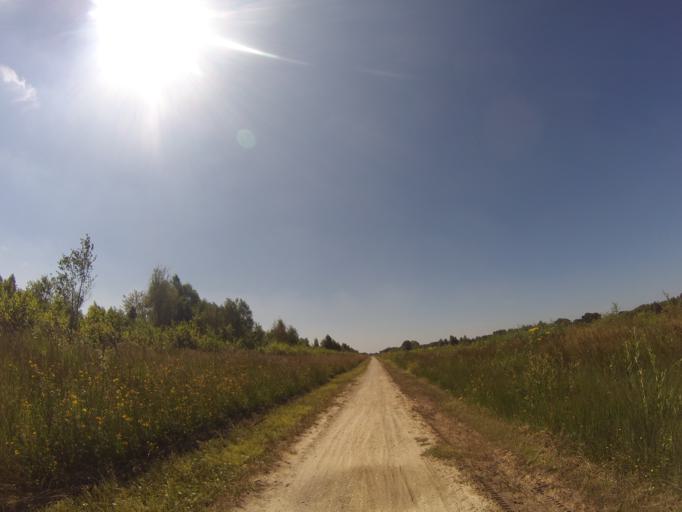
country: DE
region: Lower Saxony
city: Twist
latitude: 52.6657
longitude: 7.0153
